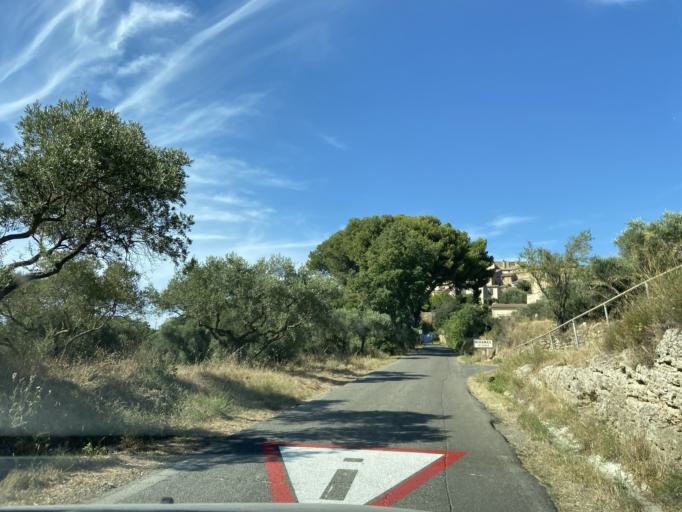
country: FR
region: Provence-Alpes-Cote d'Azur
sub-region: Departement des Bouches-du-Rhone
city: Saint-Chamas
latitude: 43.5613
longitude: 5.0234
